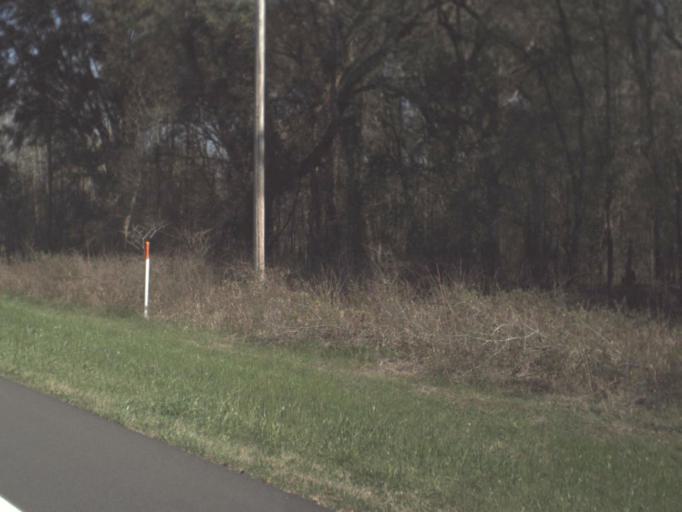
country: US
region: Florida
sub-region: Jackson County
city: Sneads
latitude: 30.7364
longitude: -85.0198
